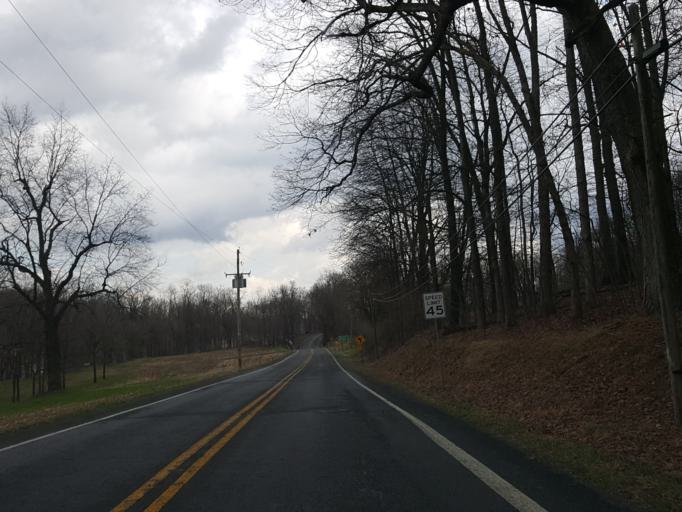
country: US
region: Pennsylvania
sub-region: Berks County
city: Robesonia
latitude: 40.3969
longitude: -76.1142
